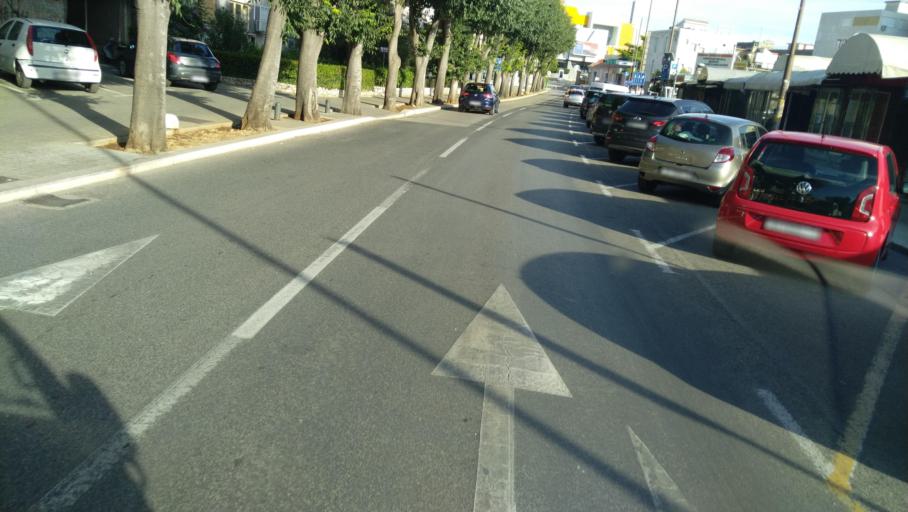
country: HR
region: Sibensko-Kniniska
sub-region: Grad Sibenik
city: Sibenik
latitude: 43.7329
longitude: 15.8959
